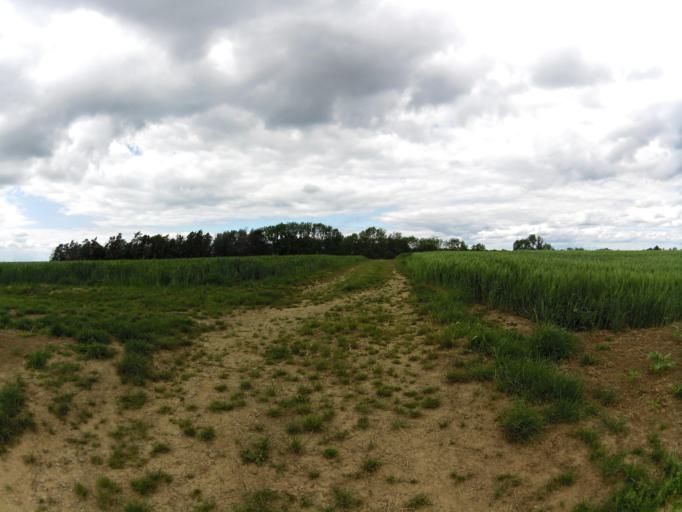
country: DE
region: Bavaria
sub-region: Regierungsbezirk Unterfranken
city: Gaukonigshofen
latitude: 49.6657
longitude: 9.9964
